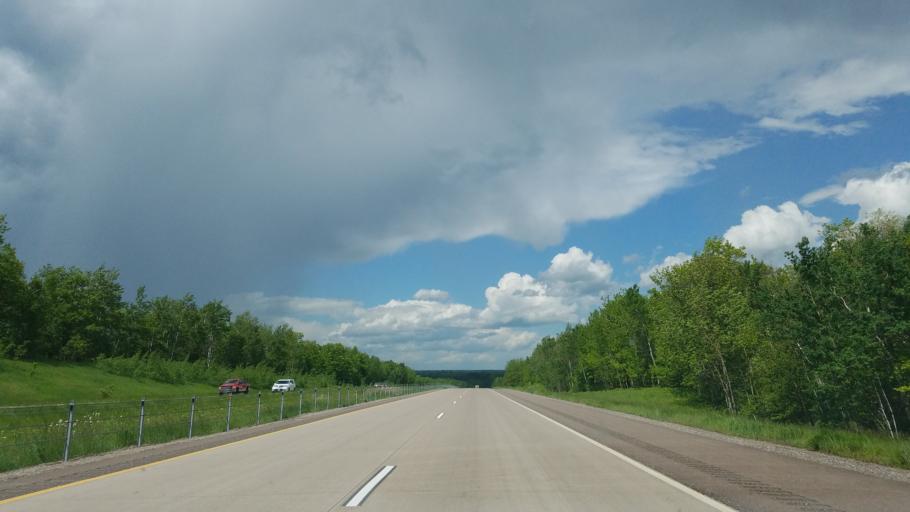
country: US
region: Minnesota
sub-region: Carlton County
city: Moose Lake
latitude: 46.4679
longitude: -92.7183
